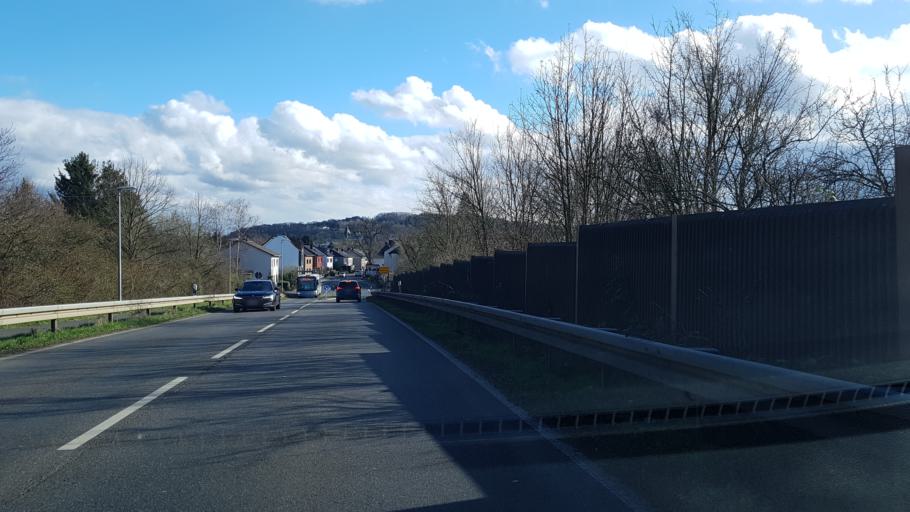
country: DE
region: North Rhine-Westphalia
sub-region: Regierungsbezirk Koln
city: Stossdorf
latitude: 50.7766
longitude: 7.2603
